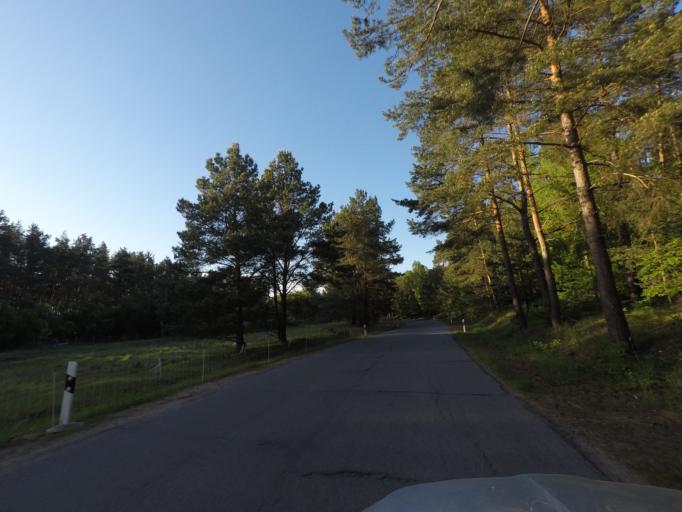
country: DE
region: Brandenburg
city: Bad Freienwalde
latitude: 52.8267
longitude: 14.0081
